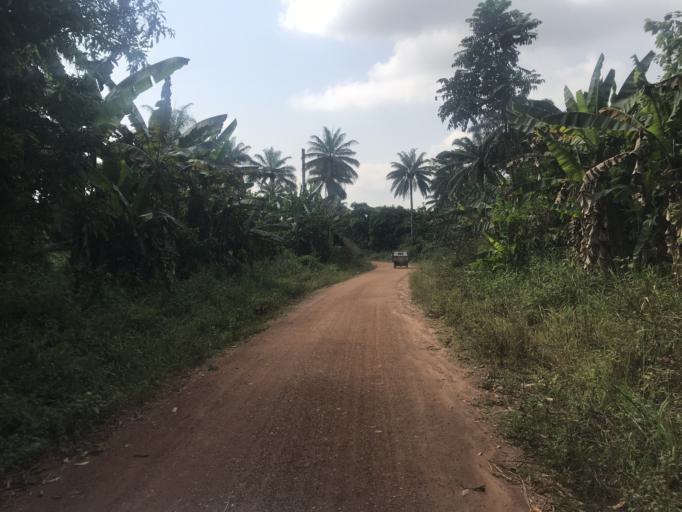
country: NG
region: Osun
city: Ikirun
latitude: 7.8553
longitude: 4.6301
